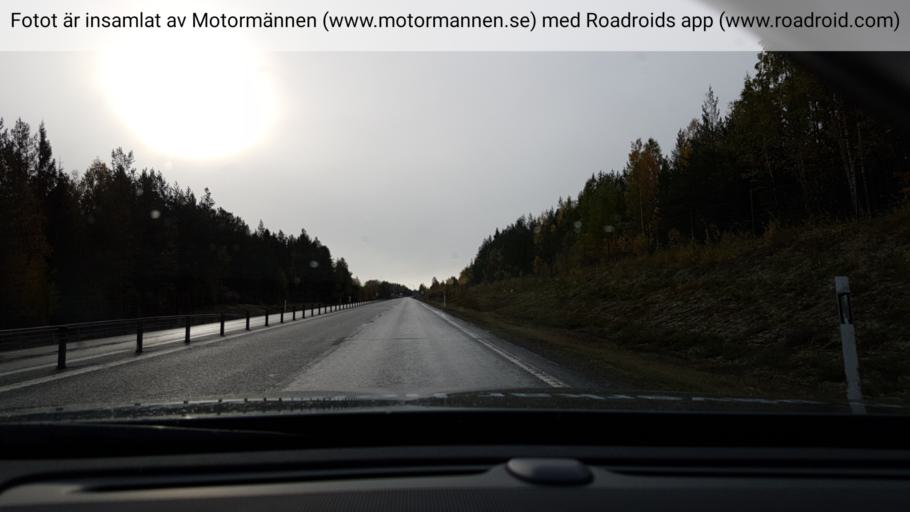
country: SE
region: Norrbotten
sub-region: Pitea Kommun
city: Pitea
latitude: 65.2482
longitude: 21.4825
